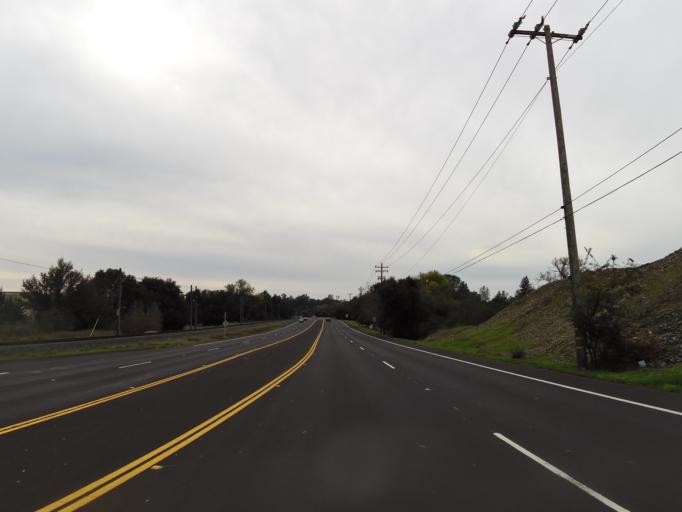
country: US
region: California
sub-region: Sacramento County
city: Folsom
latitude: 38.6681
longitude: -121.1829
